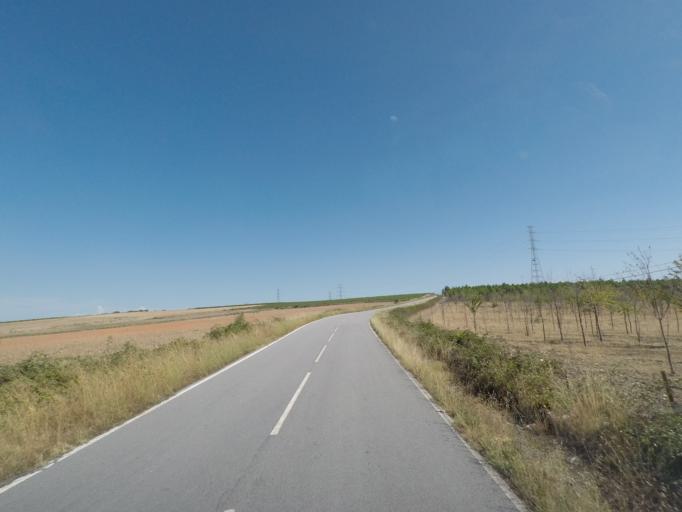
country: ES
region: Castille and Leon
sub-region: Provincia de Salamanca
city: Villarino de los Aires
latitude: 41.3228
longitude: -6.4969
